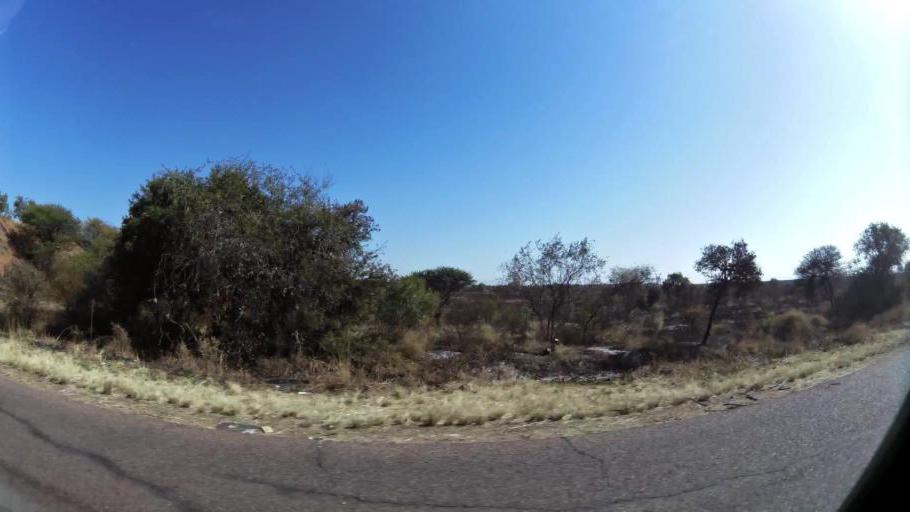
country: ZA
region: North-West
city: Ga-Rankuwa
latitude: -25.6159
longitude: 28.1126
